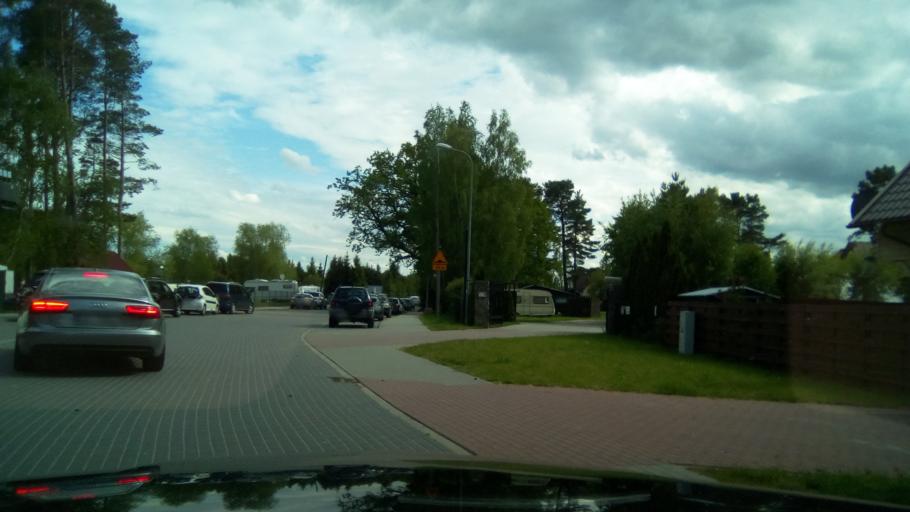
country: PL
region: Pomeranian Voivodeship
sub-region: Powiat pucki
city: Wierzchucino
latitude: 54.8289
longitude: 18.0762
